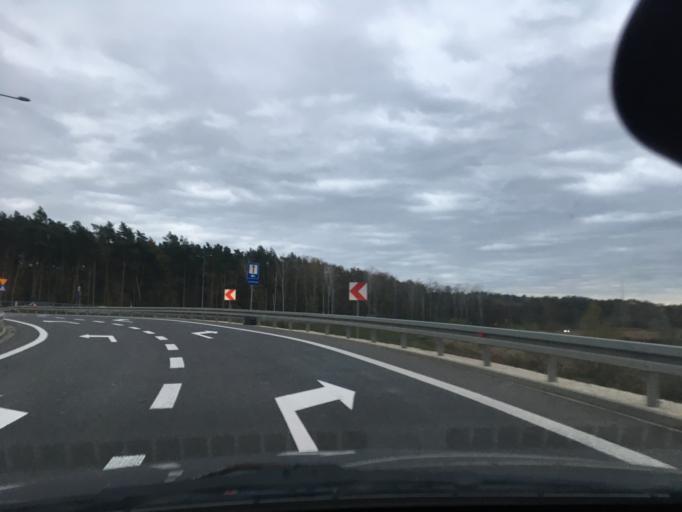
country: PL
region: Masovian Voivodeship
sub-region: Powiat pruszkowski
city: Nadarzyn
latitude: 52.1048
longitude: 20.8370
